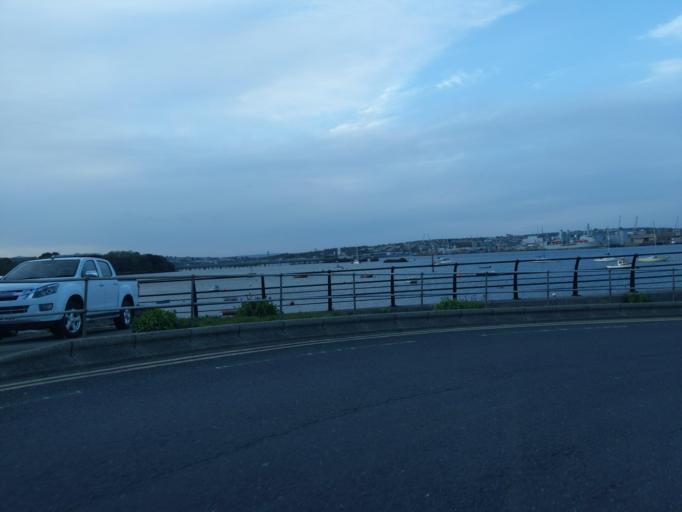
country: GB
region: England
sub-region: Cornwall
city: Torpoint
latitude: 50.3740
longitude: -4.1931
